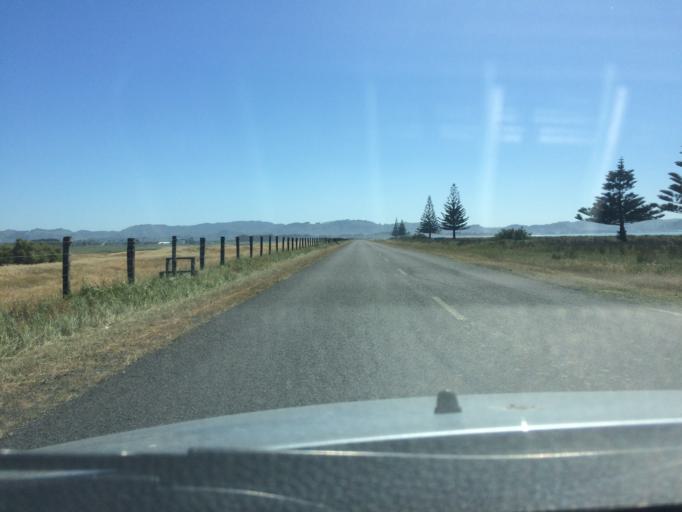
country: NZ
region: Gisborne
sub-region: Gisborne District
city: Gisborne
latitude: -38.6862
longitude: 177.9643
